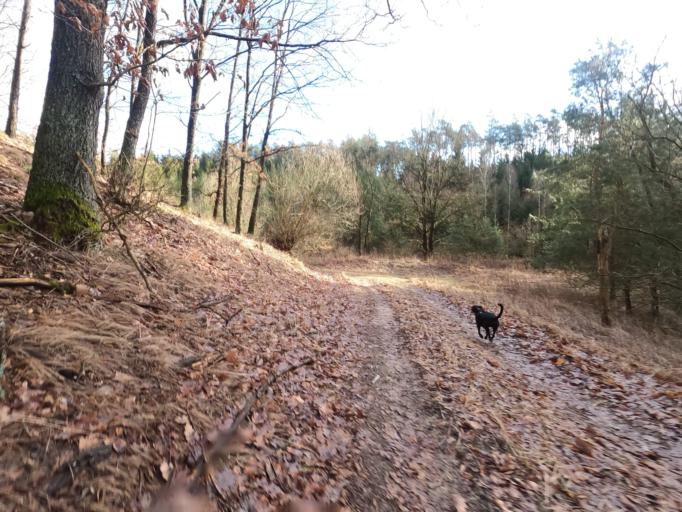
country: PL
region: Greater Poland Voivodeship
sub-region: Powiat pilski
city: Smilowo
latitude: 53.1129
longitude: 16.9601
